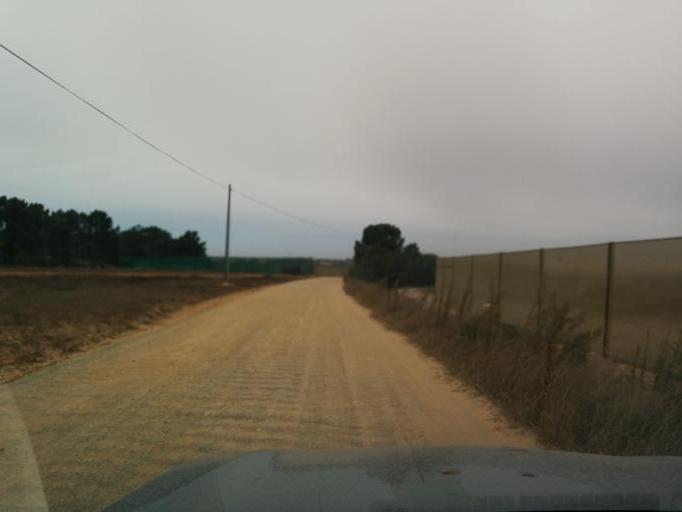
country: PT
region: Beja
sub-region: Odemira
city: Sao Teotonio
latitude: 37.5127
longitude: -8.7838
